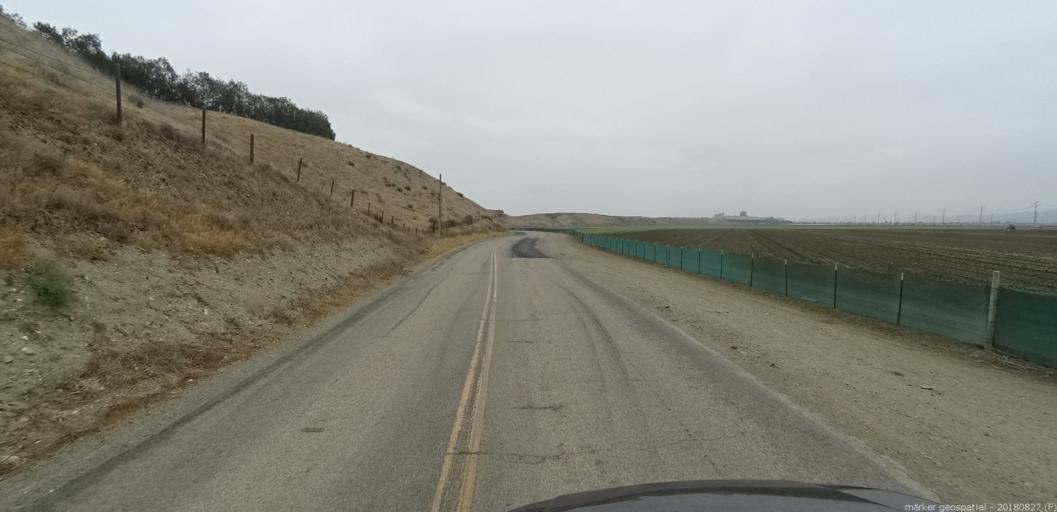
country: US
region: California
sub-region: Monterey County
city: King City
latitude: 36.2433
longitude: -121.1333
